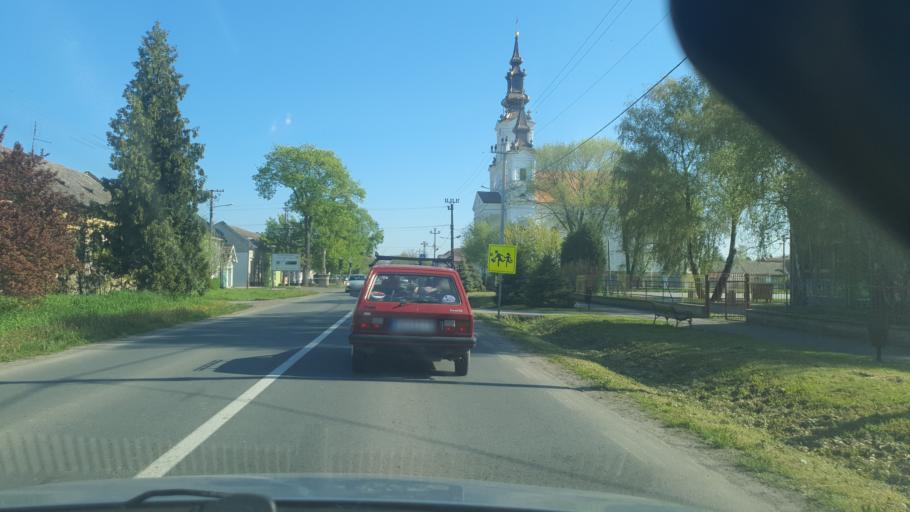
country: RS
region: Autonomna Pokrajina Vojvodina
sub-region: Zapadnobacki Okrug
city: Kula
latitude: 45.6979
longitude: 19.3806
